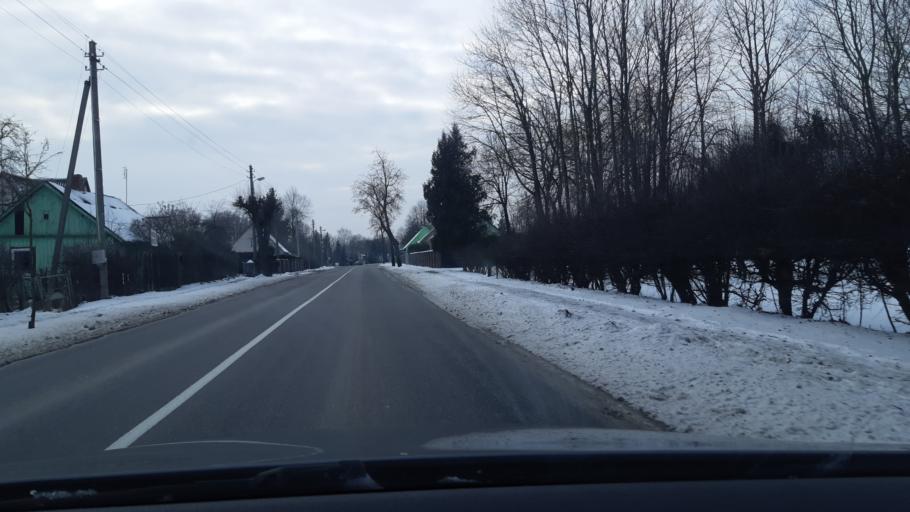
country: LT
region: Kauno apskritis
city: Kedainiai
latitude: 55.2460
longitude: 23.8394
